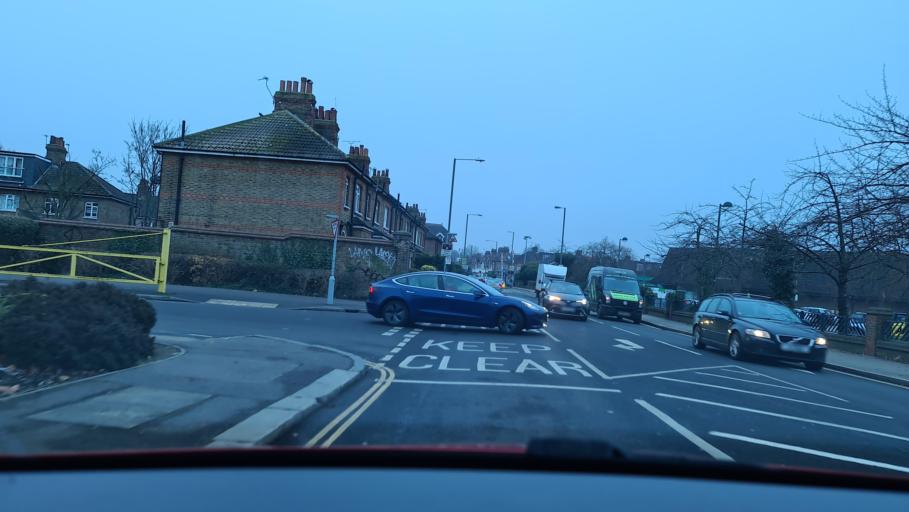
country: GB
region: England
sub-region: Greater London
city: Richmond
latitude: 51.4664
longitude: -0.2885
